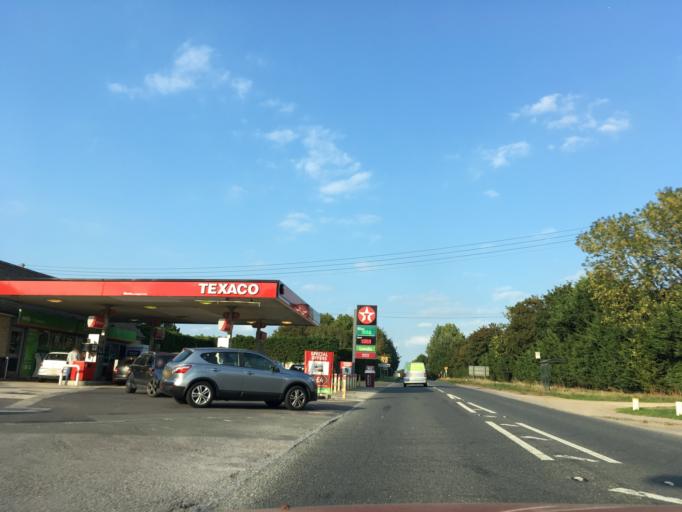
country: GB
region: England
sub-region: Gloucestershire
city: Bourton on the Water
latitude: 51.8999
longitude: -1.7499
